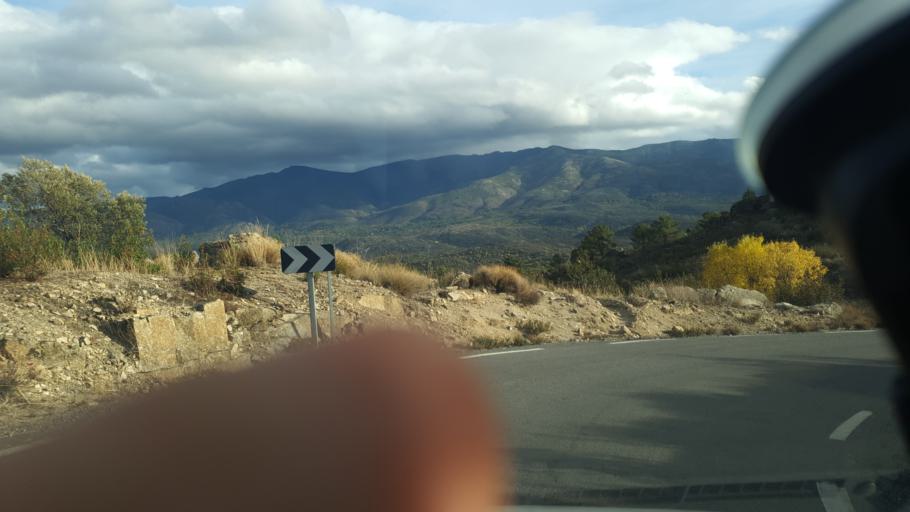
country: ES
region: Castille and Leon
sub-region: Provincia de Avila
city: Burgohondo
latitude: 40.4101
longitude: -4.8221
